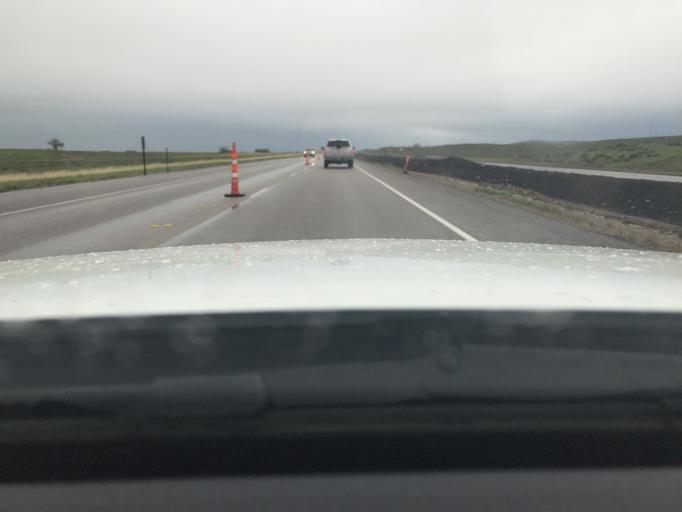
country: US
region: Wyoming
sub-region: Converse County
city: Douglas
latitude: 42.7869
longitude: -105.5346
